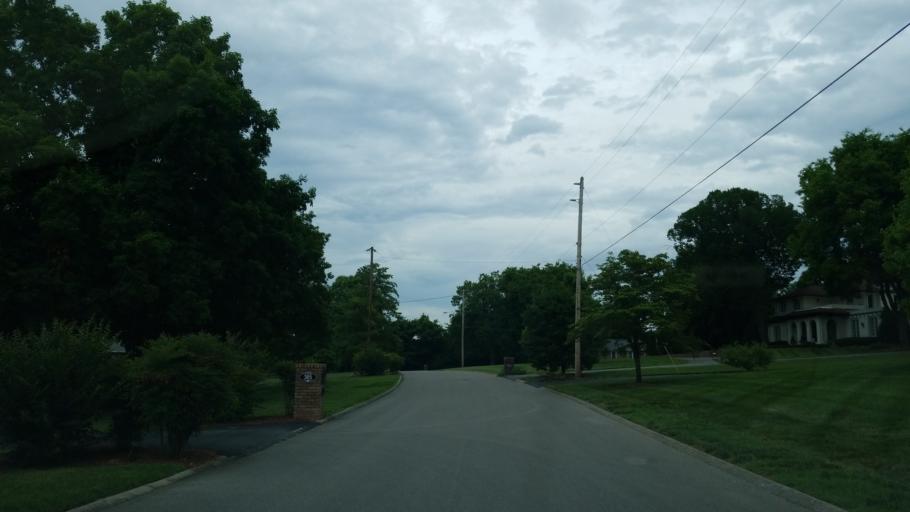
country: US
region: Tennessee
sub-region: Williamson County
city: Brentwood
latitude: 36.0299
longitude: -86.8197
